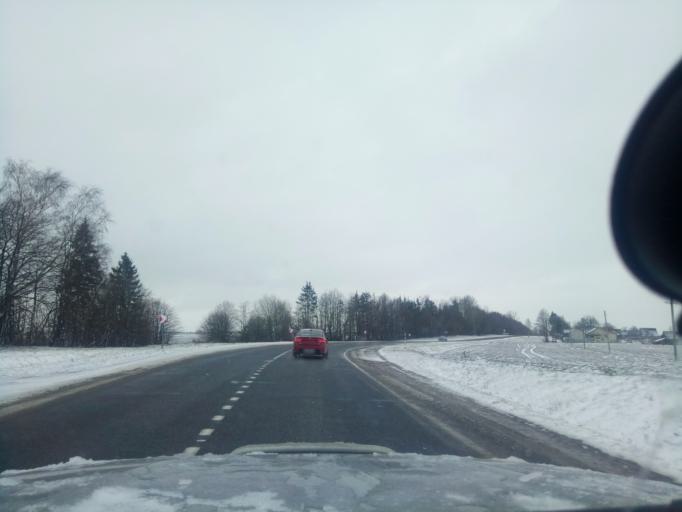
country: BY
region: Minsk
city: Nyasvizh
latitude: 53.1372
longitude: 26.6755
